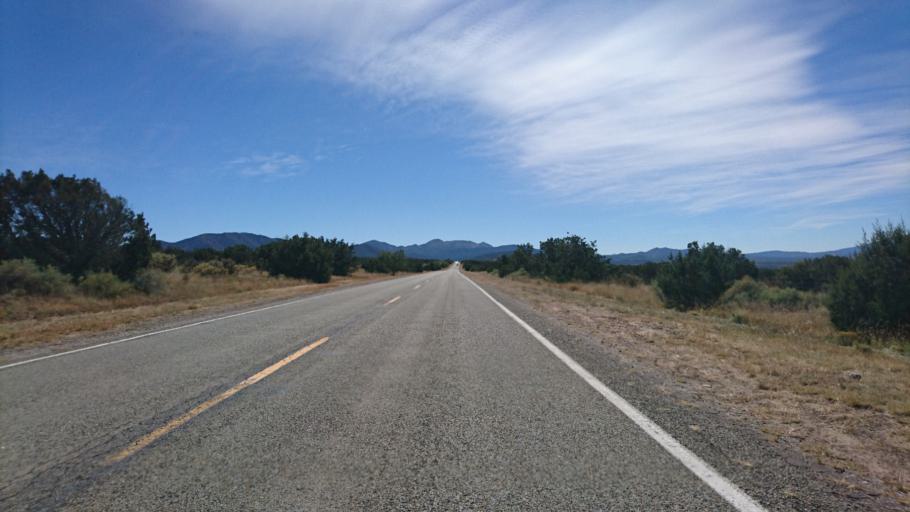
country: US
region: New Mexico
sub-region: Bernalillo County
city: Sandia Knolls
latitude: 35.3146
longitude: -106.2152
